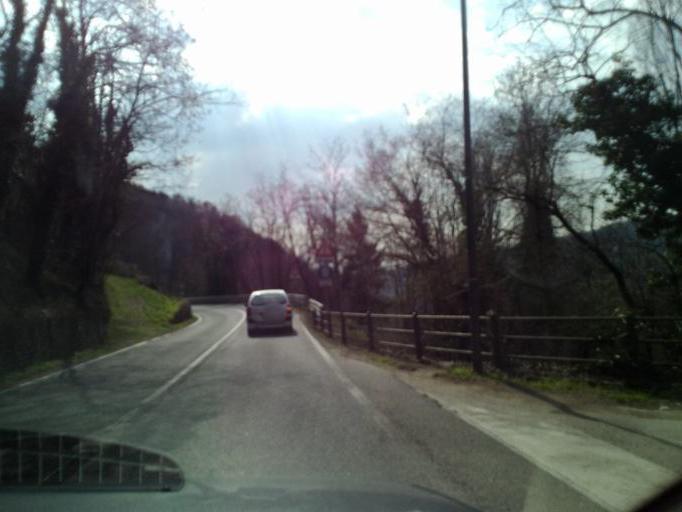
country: IT
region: Veneto
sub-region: Provincia di Verona
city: Fane
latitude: 45.5758
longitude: 10.9653
